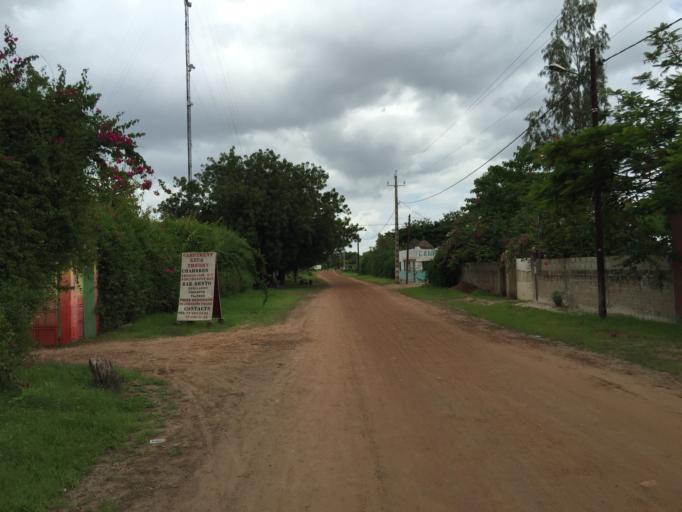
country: SN
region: Fatick
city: Sokone
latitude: 13.7870
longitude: -16.4740
